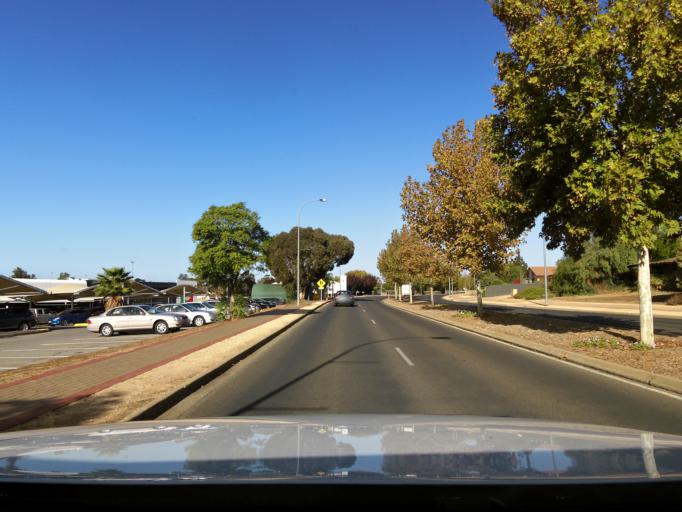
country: AU
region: South Australia
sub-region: Berri and Barmera
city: Berri
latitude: -34.2799
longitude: 140.6081
